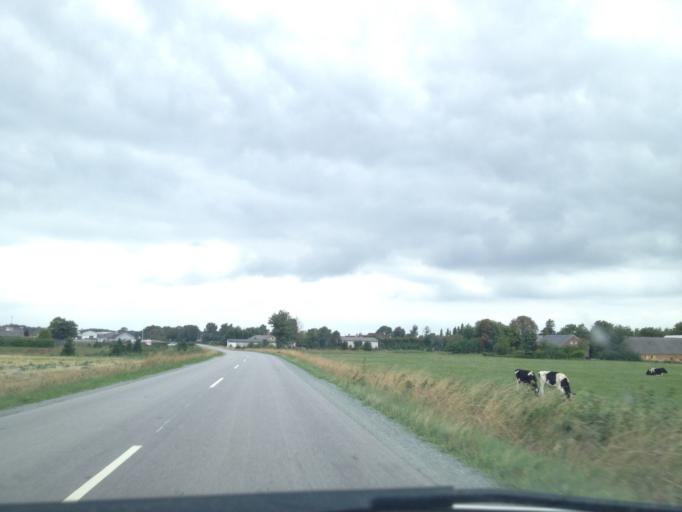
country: DK
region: South Denmark
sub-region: Kolding Kommune
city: Christiansfeld
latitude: 55.3071
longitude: 9.5128
